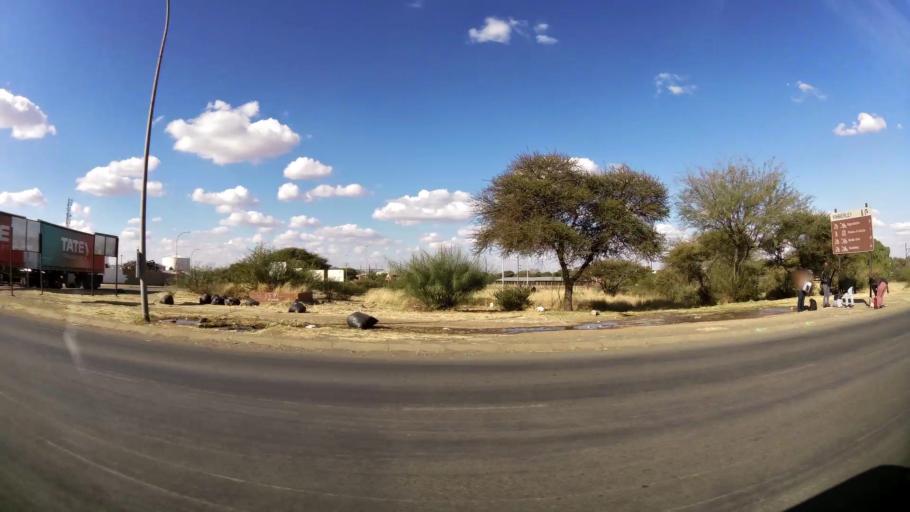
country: ZA
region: Northern Cape
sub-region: Frances Baard District Municipality
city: Kimberley
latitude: -28.7686
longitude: 24.7645
